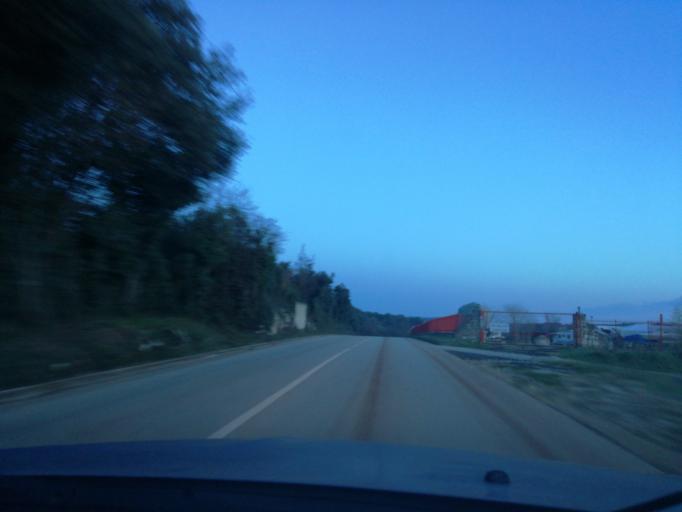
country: HR
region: Istarska
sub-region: Grad Rovinj
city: Rovinj
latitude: 45.1056
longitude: 13.6377
